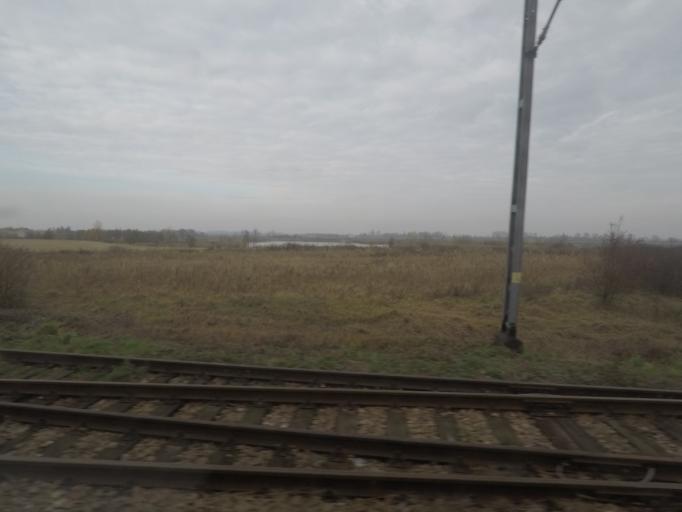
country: PL
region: Subcarpathian Voivodeship
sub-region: Powiat przemyski
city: Medyka
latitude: 49.7852
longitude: 22.8658
